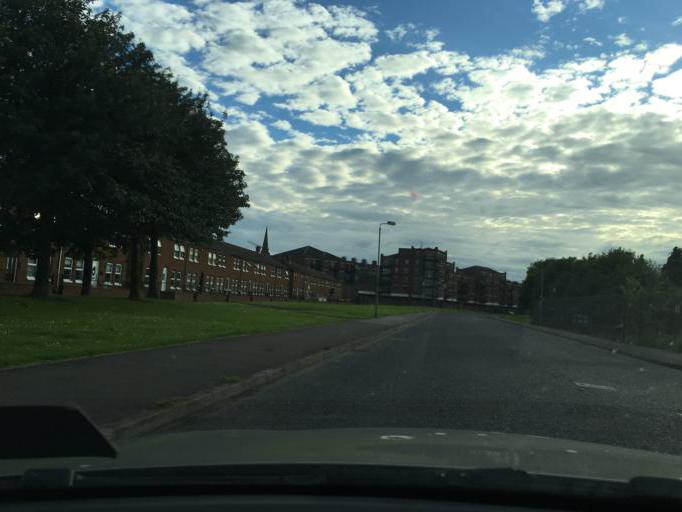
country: GB
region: Northern Ireland
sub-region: City of Belfast
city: Belfast
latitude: 54.5881
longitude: -5.9247
